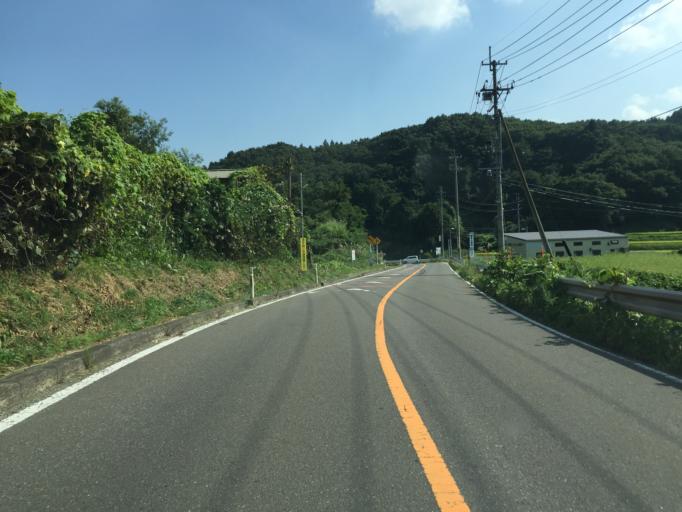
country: JP
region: Fukushima
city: Nihommatsu
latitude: 37.5884
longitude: 140.4123
